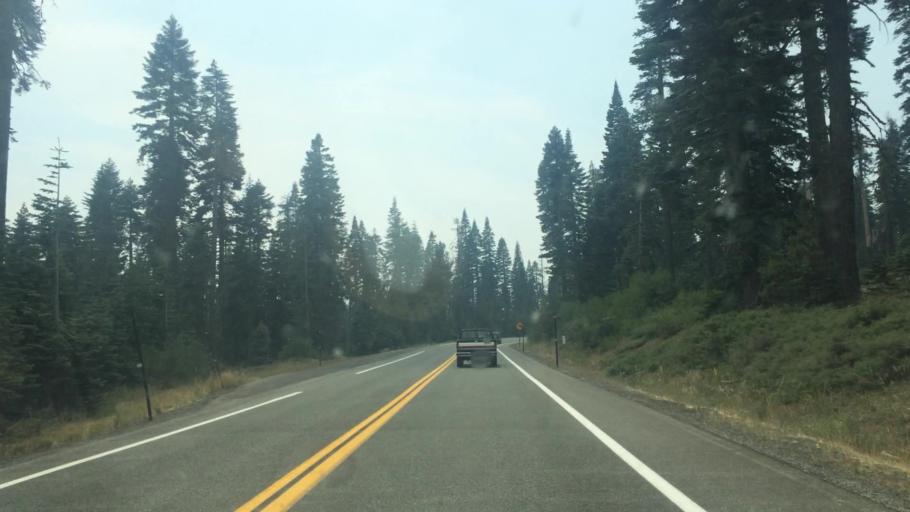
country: US
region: California
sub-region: Calaveras County
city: Arnold
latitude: 38.5892
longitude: -120.2307
